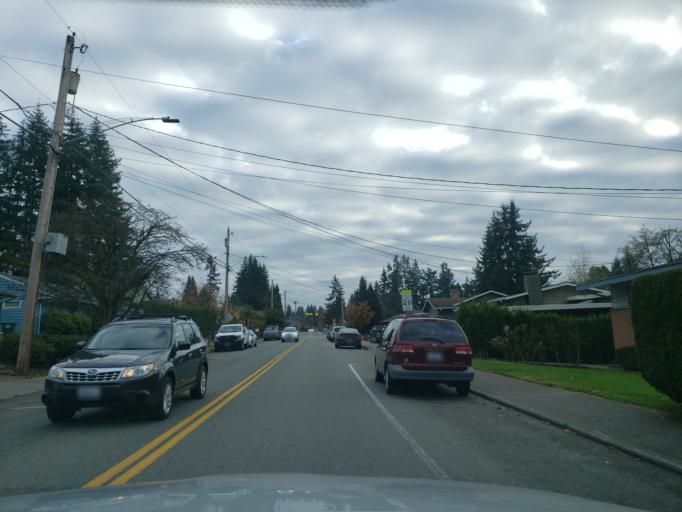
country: US
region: Washington
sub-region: Snohomish County
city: Everett
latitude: 47.9520
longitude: -122.2308
